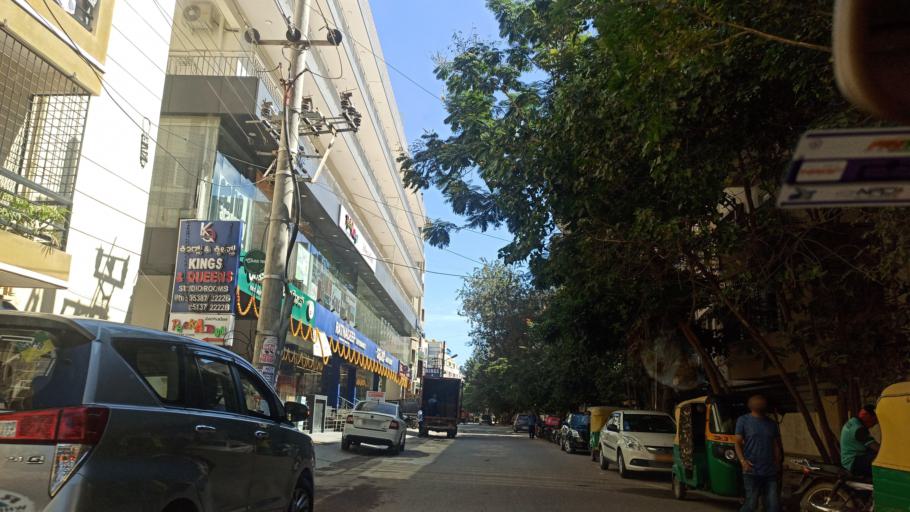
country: IN
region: Karnataka
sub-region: Bangalore Urban
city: Bangalore
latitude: 12.9272
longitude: 77.6702
